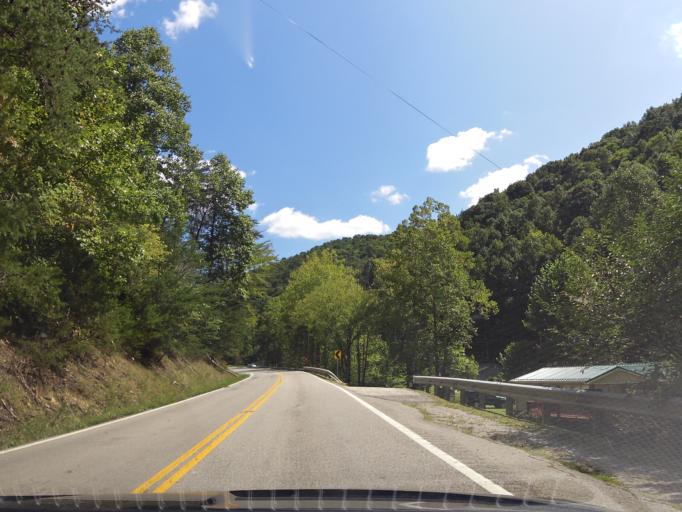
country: US
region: Kentucky
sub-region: Harlan County
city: Loyall
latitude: 36.9237
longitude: -83.3653
